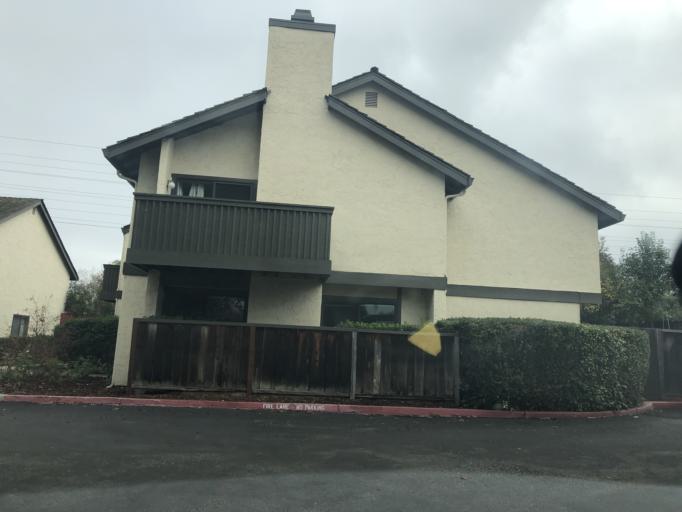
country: US
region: California
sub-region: Santa Clara County
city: Sunnyvale
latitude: 37.3938
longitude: -122.0113
